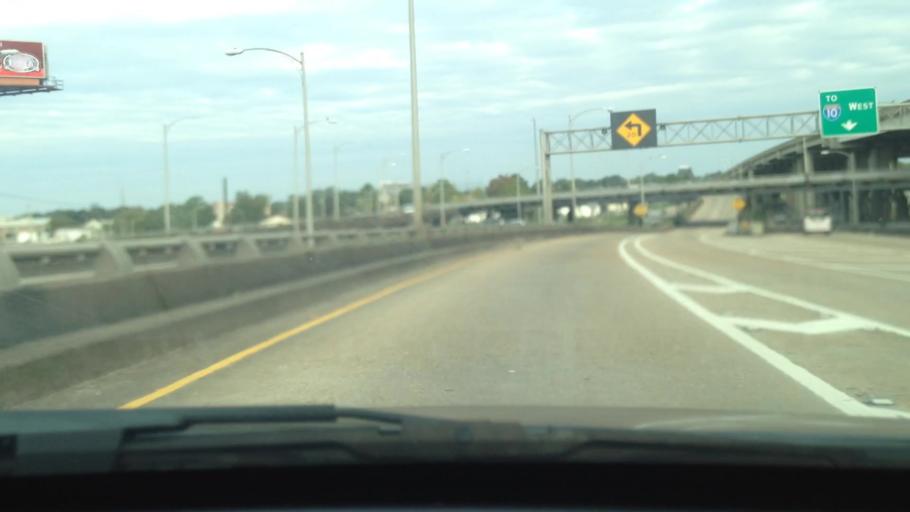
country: US
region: Louisiana
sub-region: Orleans Parish
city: New Orleans
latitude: 29.9687
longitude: -90.1091
